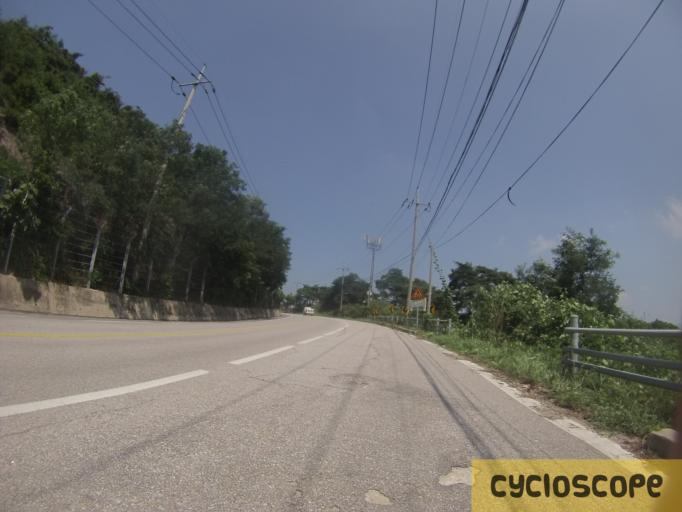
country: KR
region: Jeollabuk-do
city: Puan
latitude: 35.6523
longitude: 126.5470
